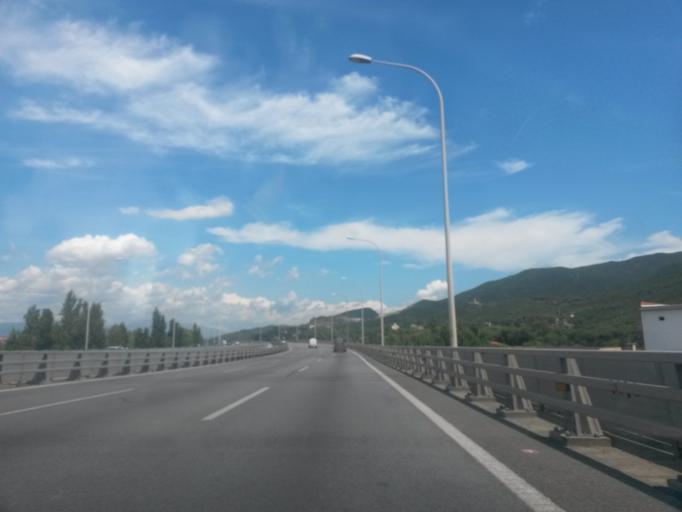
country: ES
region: Catalonia
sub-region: Provincia de Barcelona
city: Montcada i Reixac
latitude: 41.4894
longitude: 2.1872
